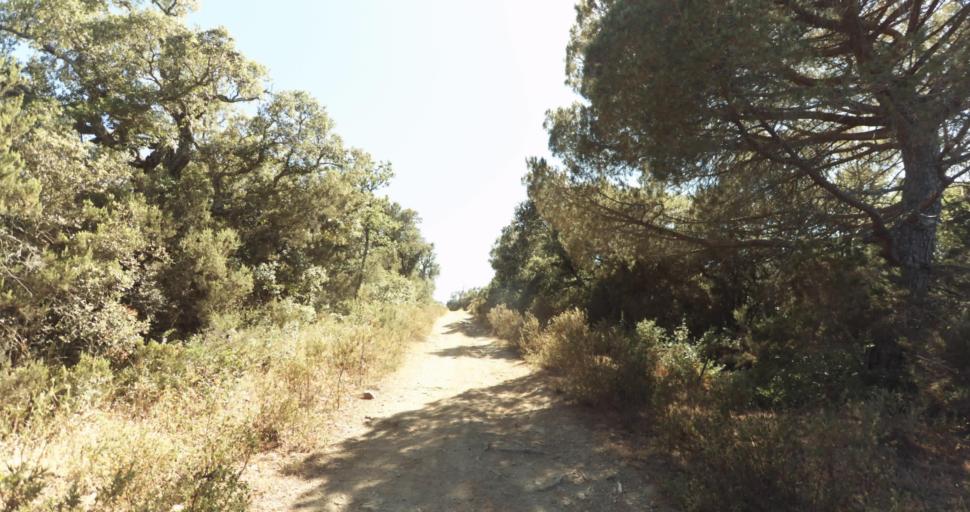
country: FR
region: Provence-Alpes-Cote d'Azur
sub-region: Departement du Var
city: Gassin
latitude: 43.2487
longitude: 6.5855
